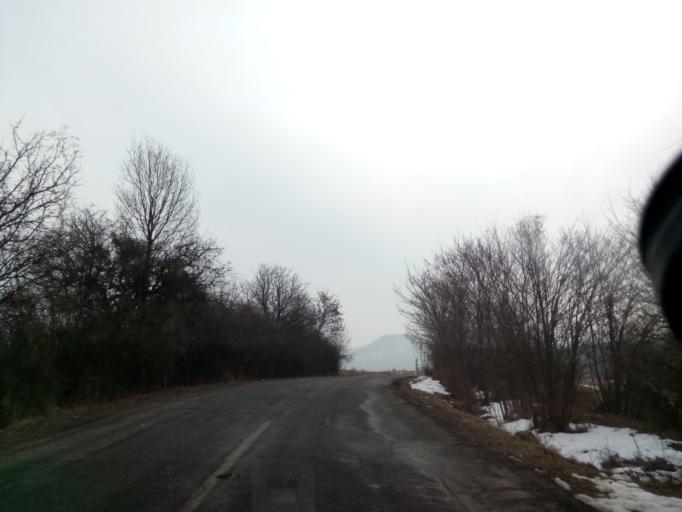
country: HU
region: Borsod-Abauj-Zemplen
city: Gonc
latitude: 48.4859
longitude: 21.3883
